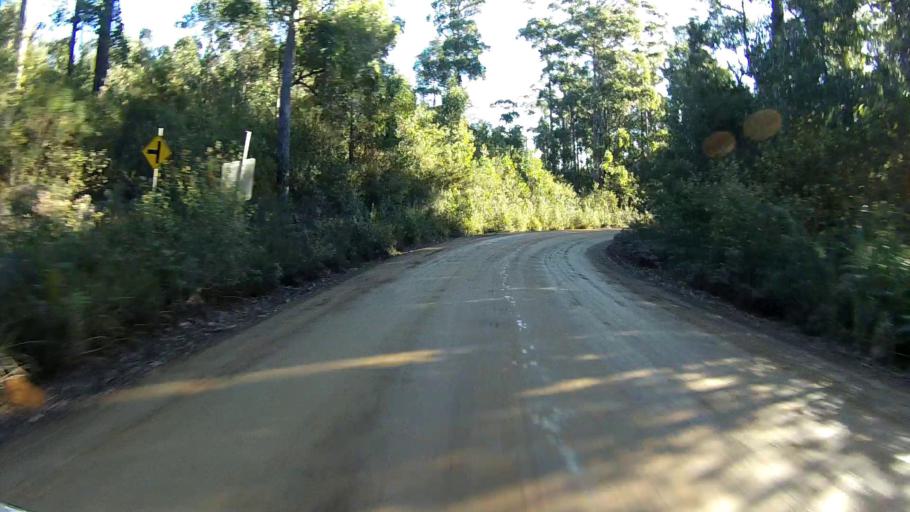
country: AU
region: Tasmania
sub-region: Clarence
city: Sandford
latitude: -43.1164
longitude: 147.9118
